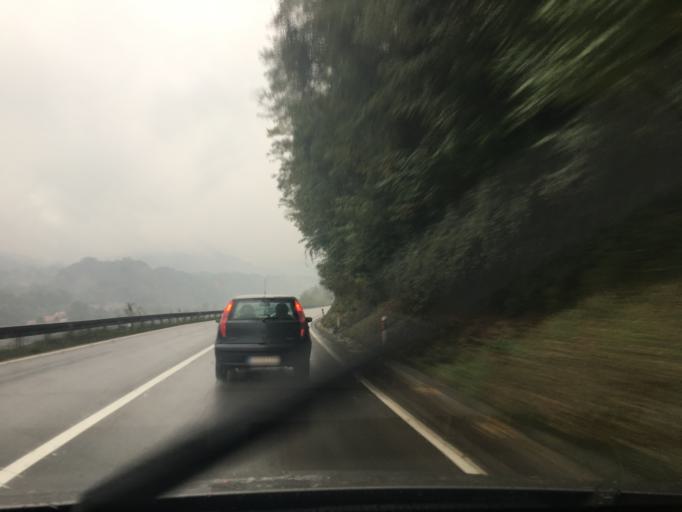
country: RS
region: Central Serbia
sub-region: Pcinjski Okrug
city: Vladicin Han
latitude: 42.7869
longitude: 22.0922
